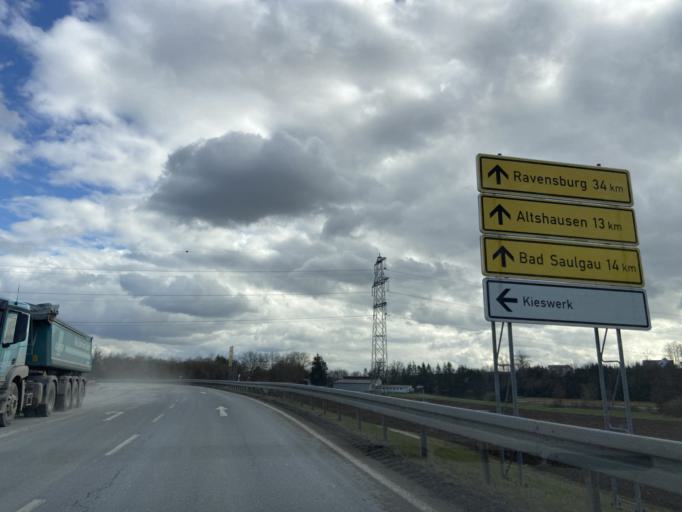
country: DE
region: Baden-Wuerttemberg
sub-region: Tuebingen Region
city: Ostrach
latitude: 47.9599
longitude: 9.3753
